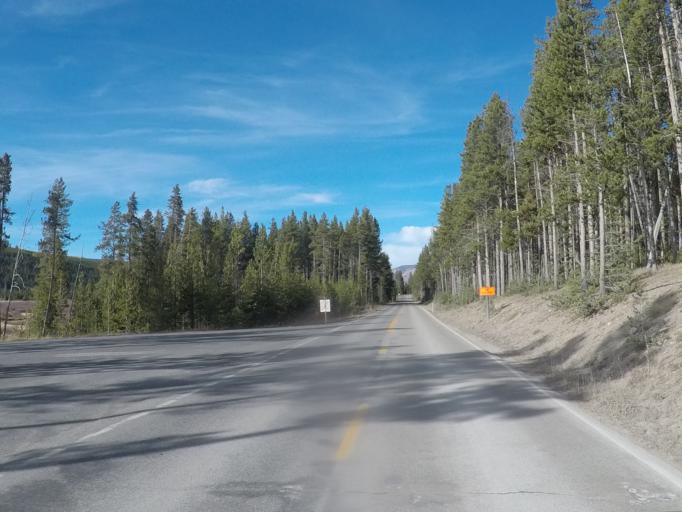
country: US
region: Montana
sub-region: Gallatin County
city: West Yellowstone
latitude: 44.8597
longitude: -110.7360
